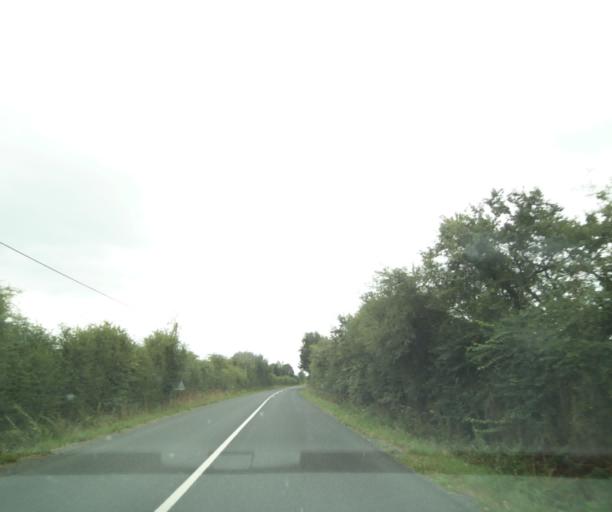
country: FR
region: Pays de la Loire
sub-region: Departement de la Sarthe
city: Precigne
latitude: 47.7610
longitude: -0.3135
